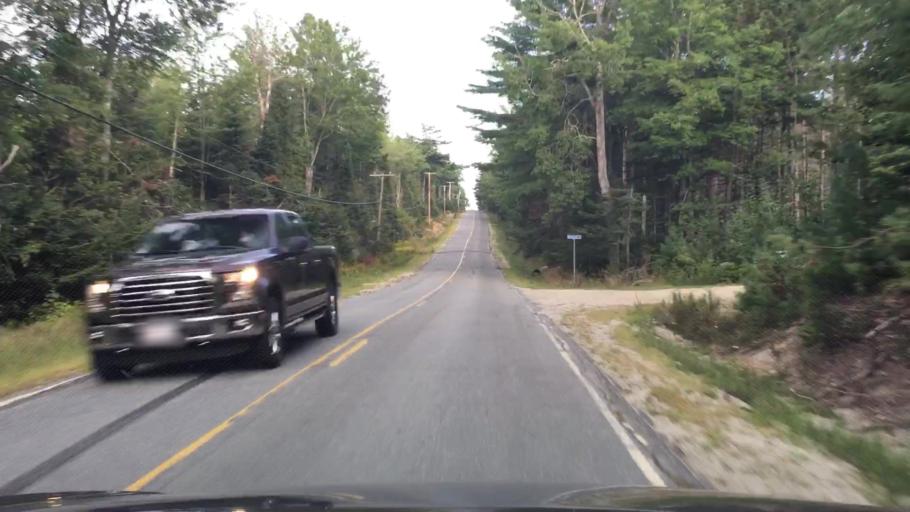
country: US
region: Maine
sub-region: Hancock County
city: Surry
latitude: 44.5002
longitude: -68.5621
